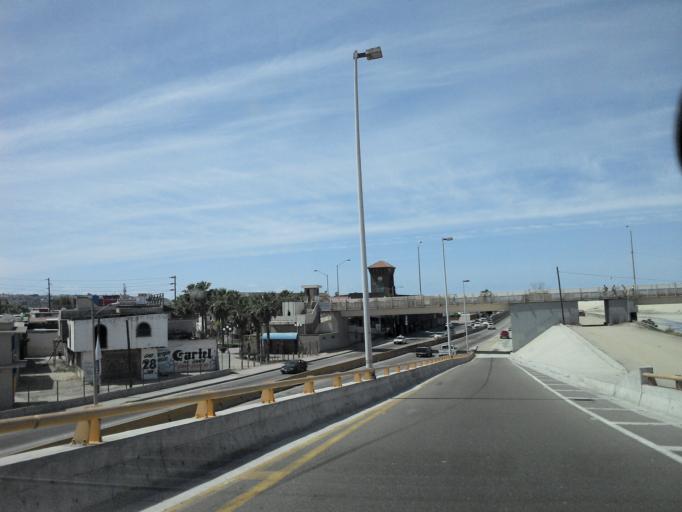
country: MX
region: Baja California
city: Tijuana
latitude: 32.5375
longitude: -117.0322
